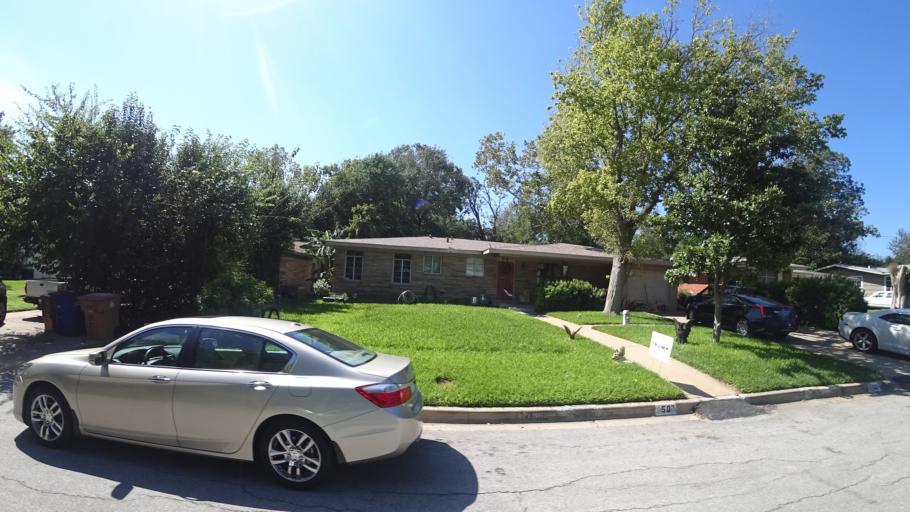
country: US
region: Texas
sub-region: Travis County
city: Austin
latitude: 30.3116
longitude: -97.6967
